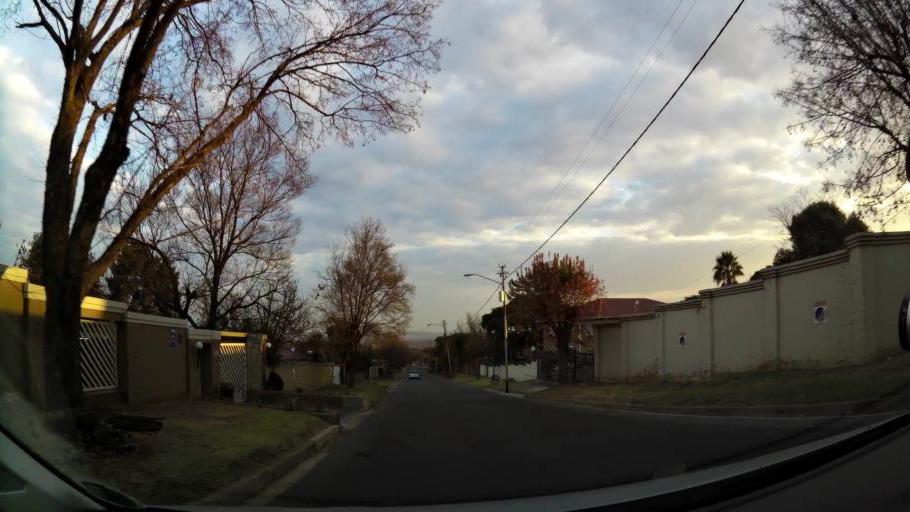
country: ZA
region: Gauteng
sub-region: Ekurhuleni Metropolitan Municipality
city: Germiston
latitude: -26.1901
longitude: 28.1445
